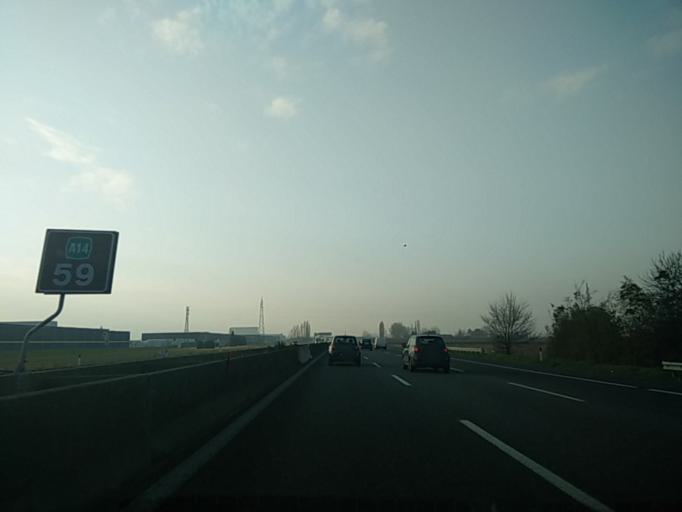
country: IT
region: Emilia-Romagna
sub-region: Provincia di Ravenna
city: Faenza
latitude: 44.3283
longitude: 11.8937
